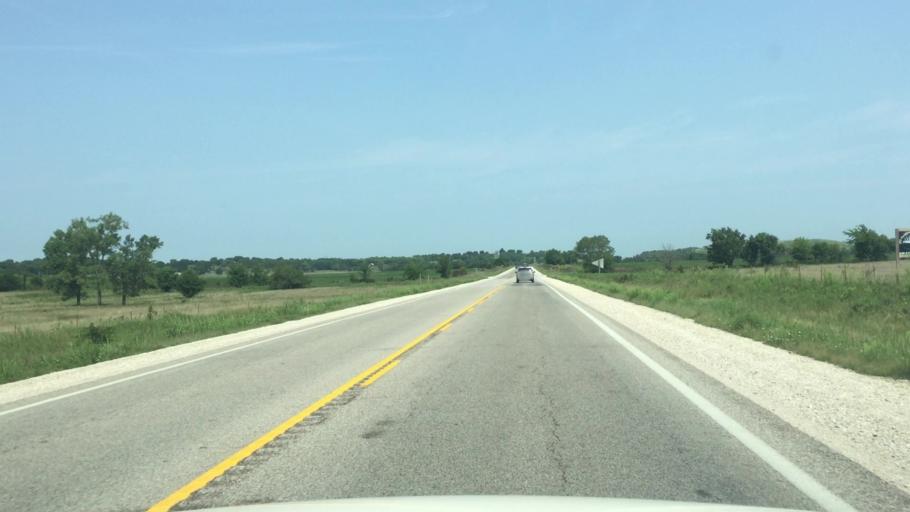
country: US
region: Kansas
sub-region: Montgomery County
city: Cherryvale
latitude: 37.1925
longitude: -95.5809
